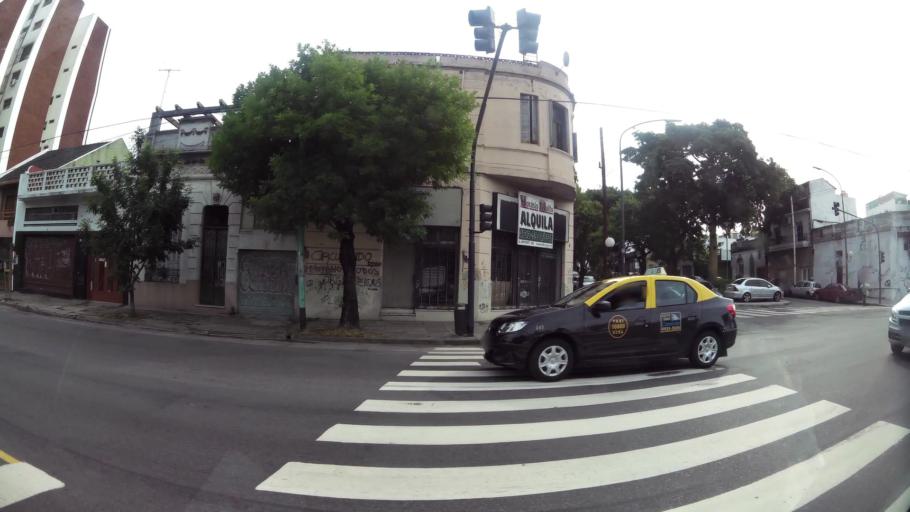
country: AR
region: Buenos Aires F.D.
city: Villa Santa Rita
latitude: -34.6392
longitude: -58.4658
